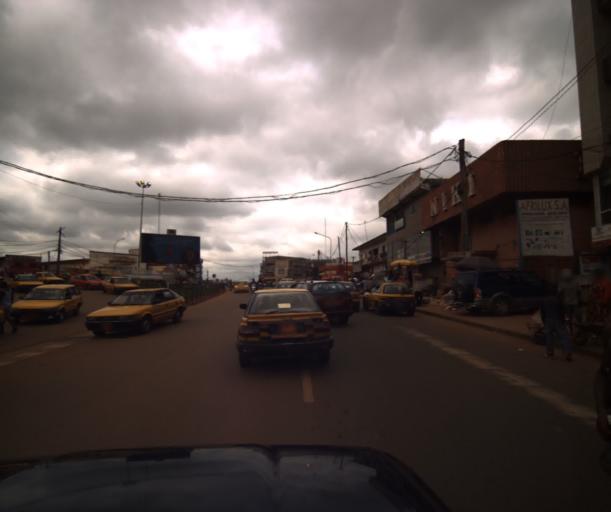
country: CM
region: Centre
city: Yaounde
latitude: 3.8518
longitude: 11.5218
